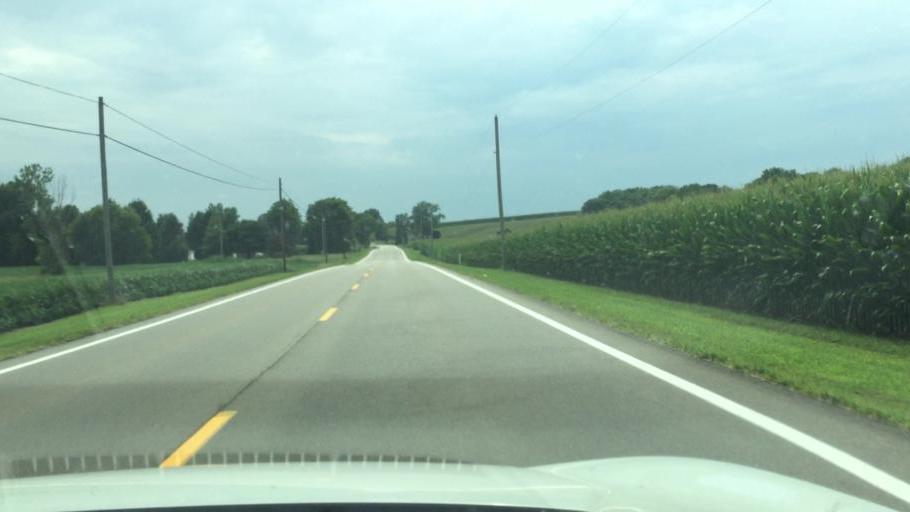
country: US
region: Ohio
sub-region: Clark County
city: Northridge
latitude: 40.0217
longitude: -83.6646
